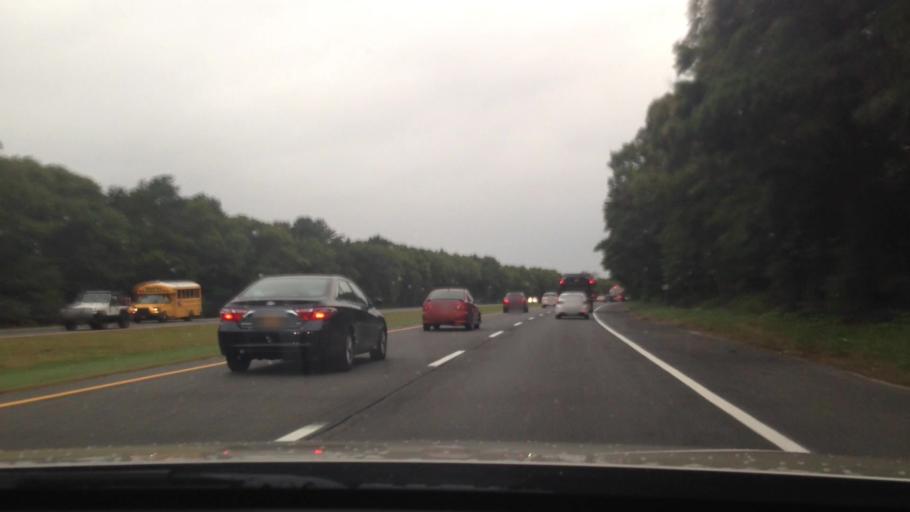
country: US
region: New York
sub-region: Suffolk County
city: Holtsville
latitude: 40.7835
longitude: -73.0509
